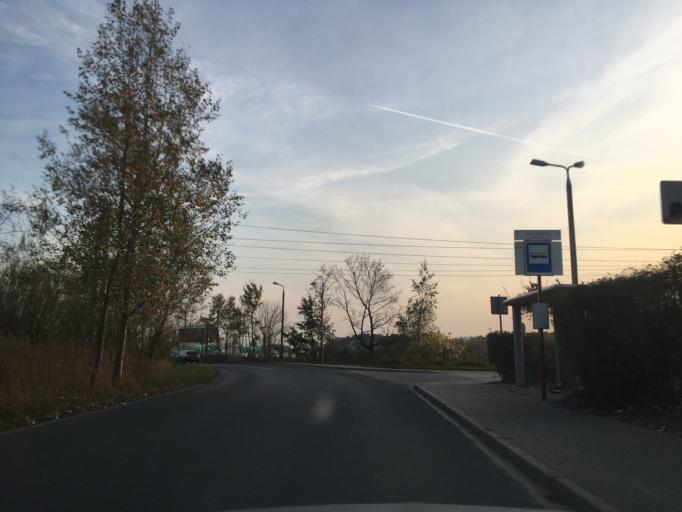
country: PL
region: Masovian Voivodeship
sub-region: Powiat piaseczynski
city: Lesznowola
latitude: 52.0762
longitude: 20.8909
